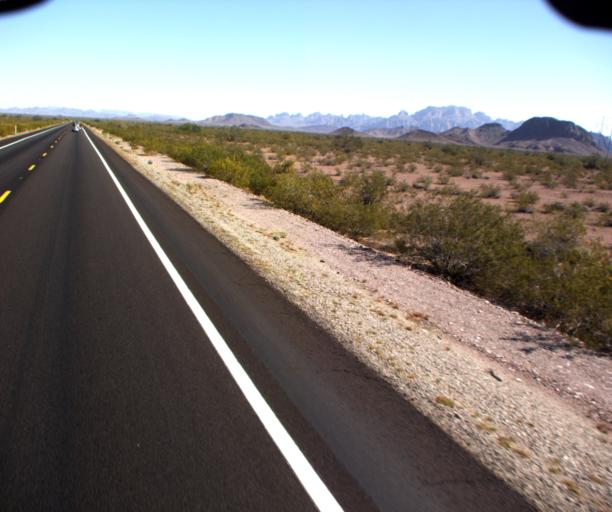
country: US
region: Arizona
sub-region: La Paz County
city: Quartzsite
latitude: 33.2874
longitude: -114.2275
